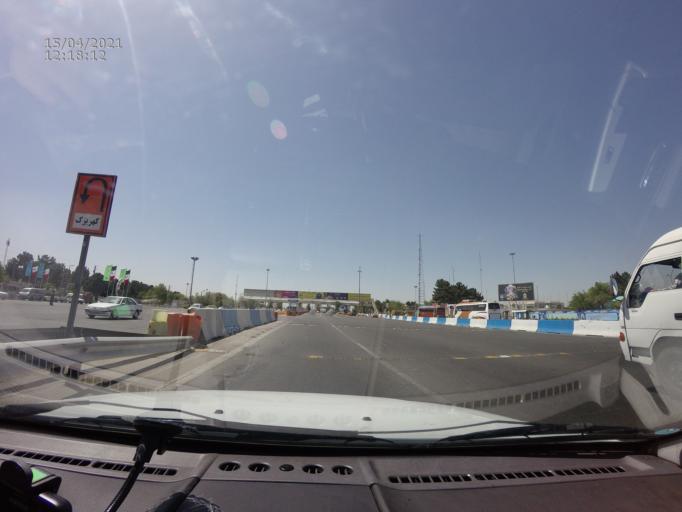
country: IR
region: Tehran
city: Shahrak-e Emam Hasan-e Mojtaba
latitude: 35.5433
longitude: 51.3551
